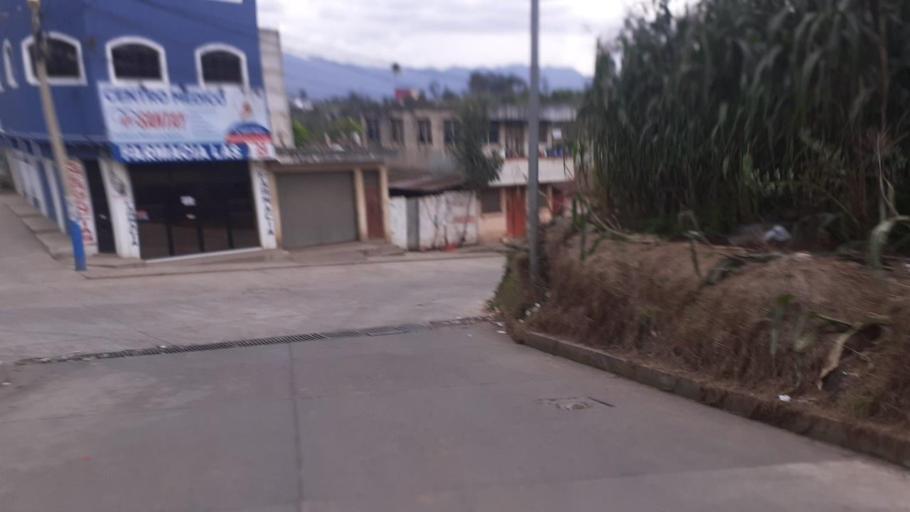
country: GT
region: Quetzaltenango
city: Ostuncalco
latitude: 14.8717
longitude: -91.6185
